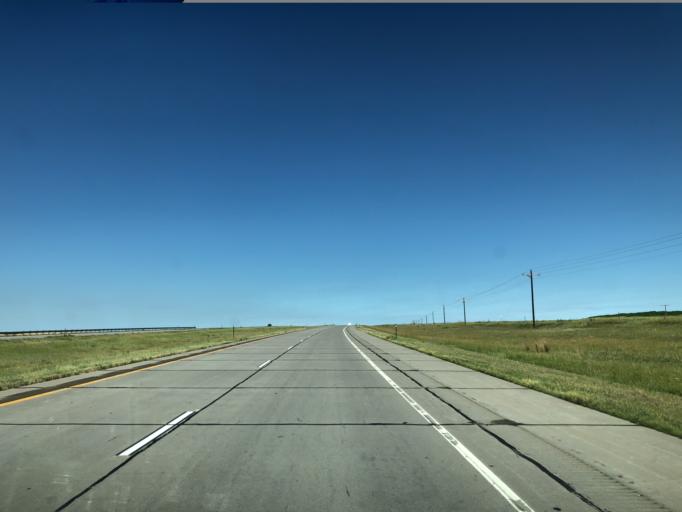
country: US
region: Colorado
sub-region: Kit Carson County
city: Burlington
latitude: 39.2931
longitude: -102.4556
